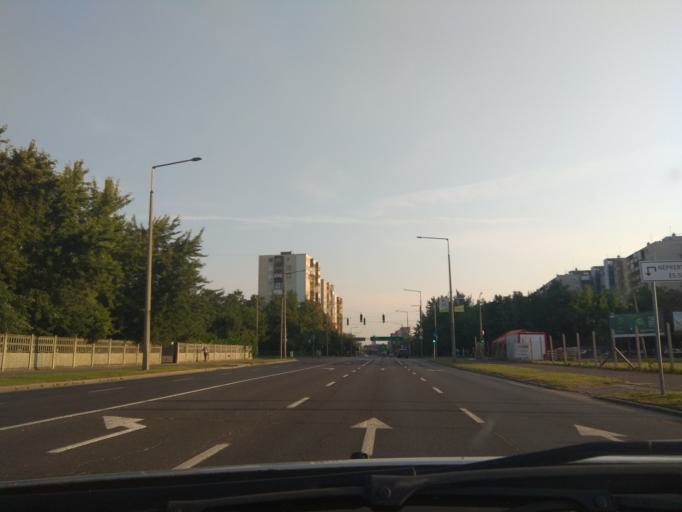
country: HU
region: Borsod-Abauj-Zemplen
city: Miskolc
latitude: 48.0969
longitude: 20.7926
